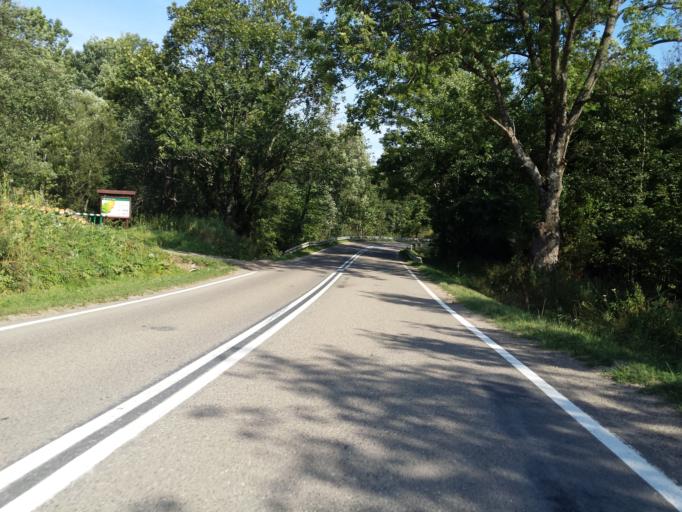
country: PL
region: Subcarpathian Voivodeship
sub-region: Powiat leski
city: Cisna
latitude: 49.2529
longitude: 22.2852
